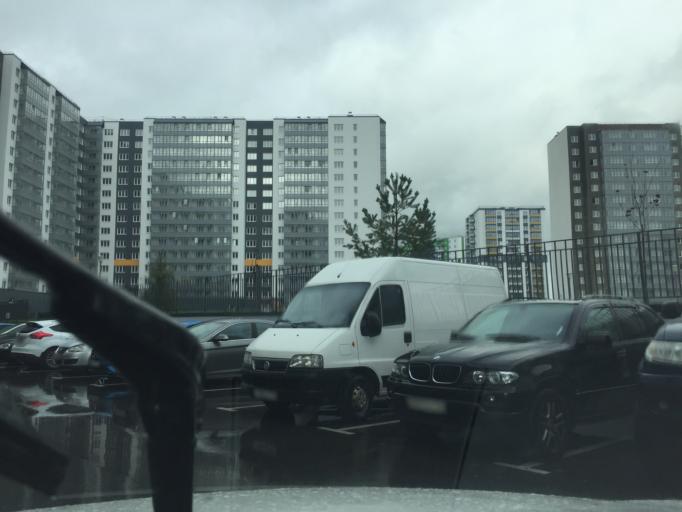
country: RU
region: St.-Petersburg
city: Gorelovo
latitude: 59.7889
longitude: 30.1656
